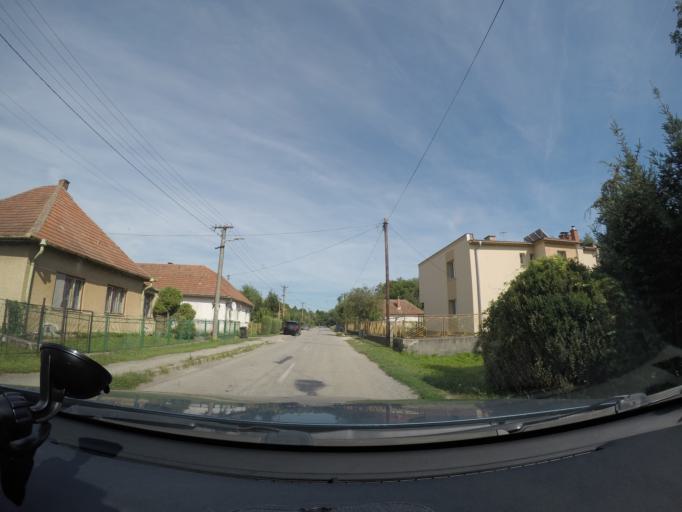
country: SK
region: Nitriansky
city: Banovce nad Bebravou
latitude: 48.7368
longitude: 18.1628
